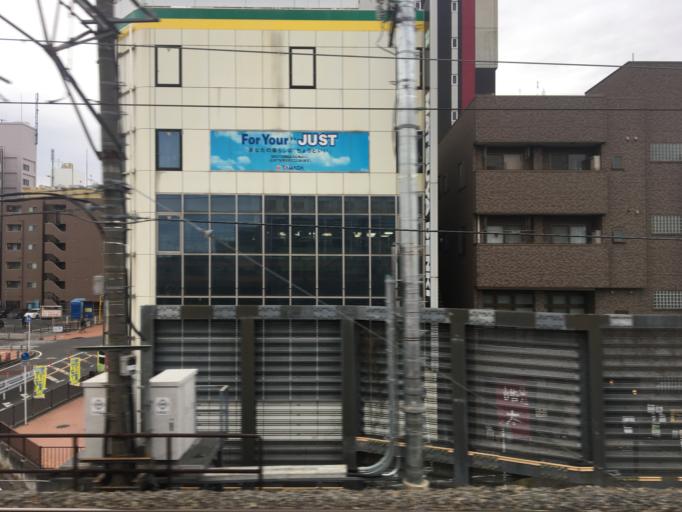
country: JP
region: Chiba
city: Nagareyama
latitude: 35.8389
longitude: 139.9032
